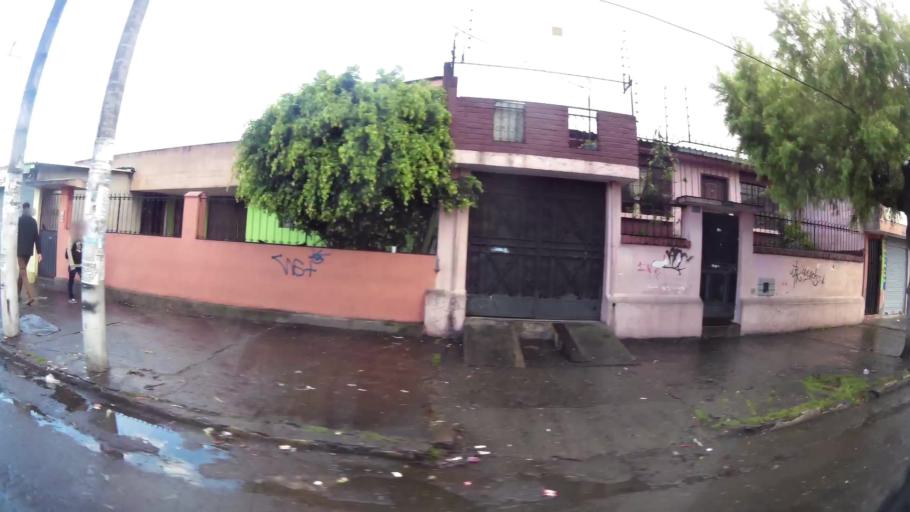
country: EC
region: Pichincha
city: Quito
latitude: -0.1139
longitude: -78.4914
